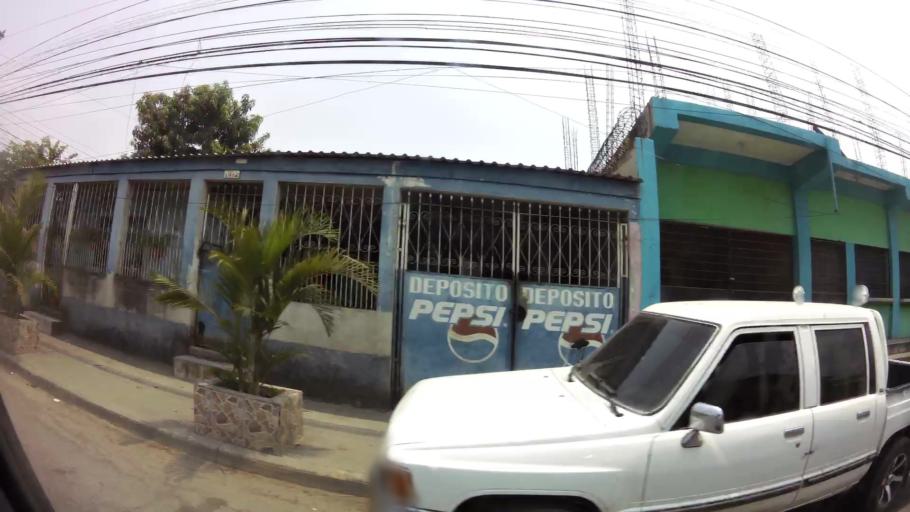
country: HN
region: Cortes
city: San Pedro Sula
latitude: 15.4846
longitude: -88.0074
